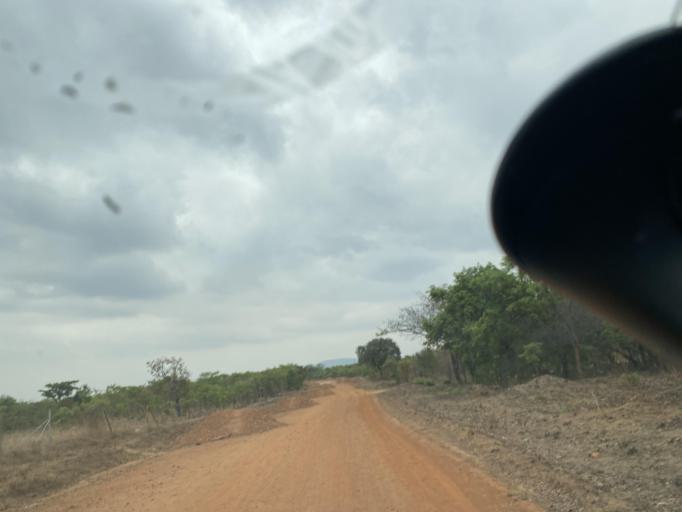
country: ZM
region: Lusaka
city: Chongwe
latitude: -15.2488
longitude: 28.7268
